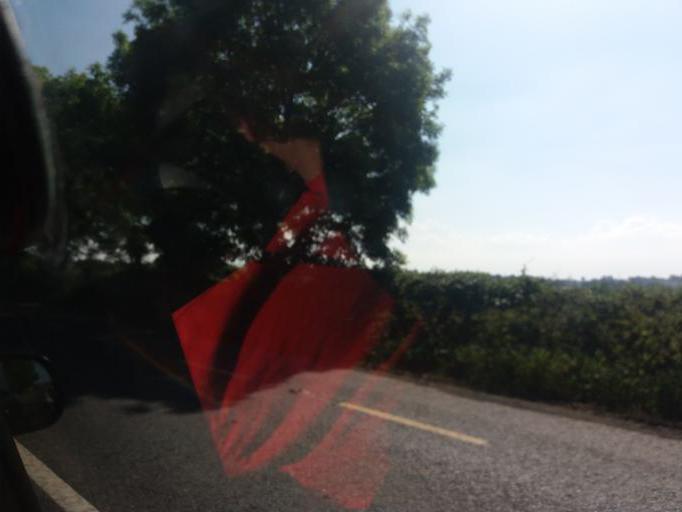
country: IE
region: Leinster
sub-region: An Mhi
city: Slane
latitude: 53.6895
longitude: -6.5413
